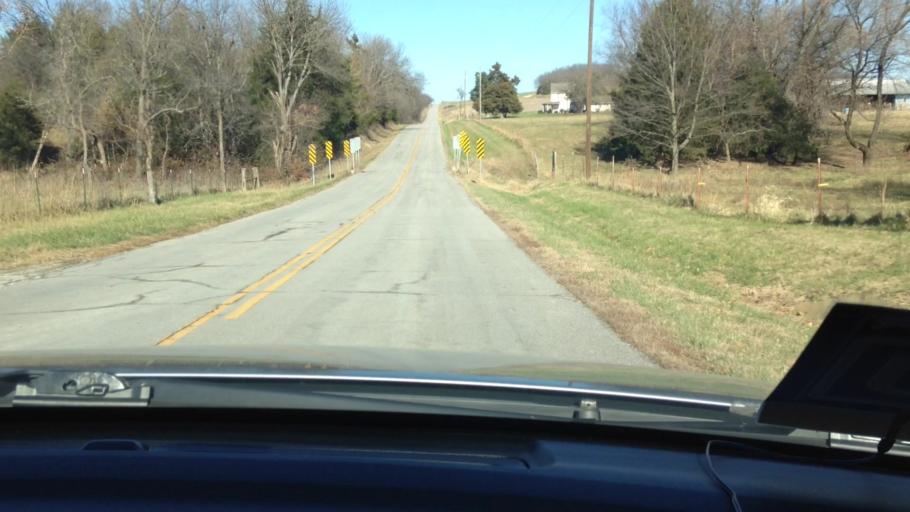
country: US
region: Missouri
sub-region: Platte County
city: Weston
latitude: 39.4683
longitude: -94.9007
